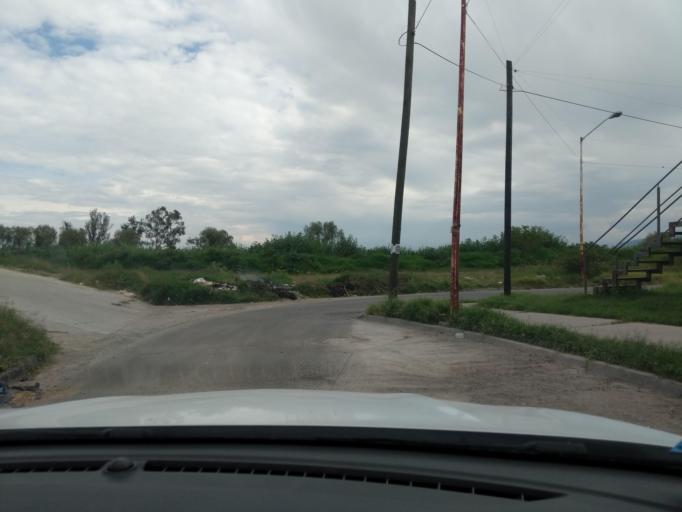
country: MX
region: Jalisco
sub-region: El Salto
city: Galaxia Bonito Jalisco
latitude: 20.5046
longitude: -103.1906
